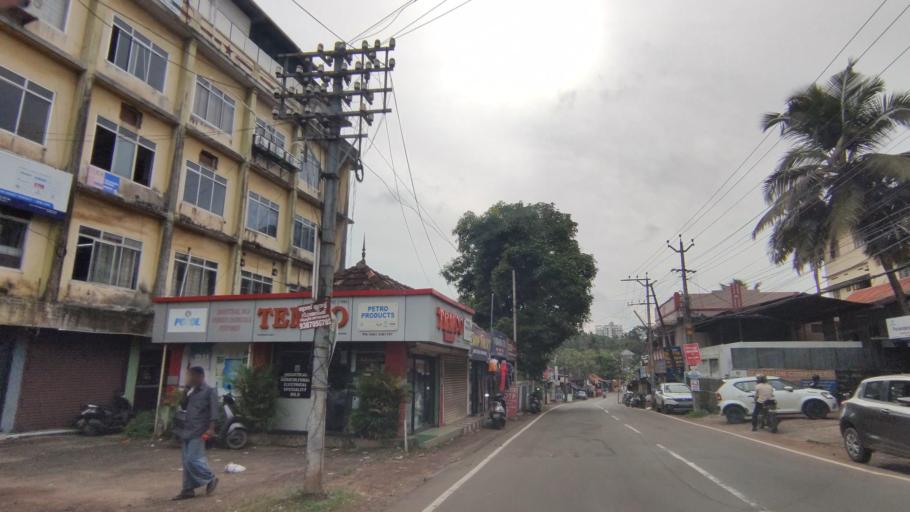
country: IN
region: Kerala
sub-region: Kottayam
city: Kottayam
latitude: 9.5876
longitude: 76.5194
